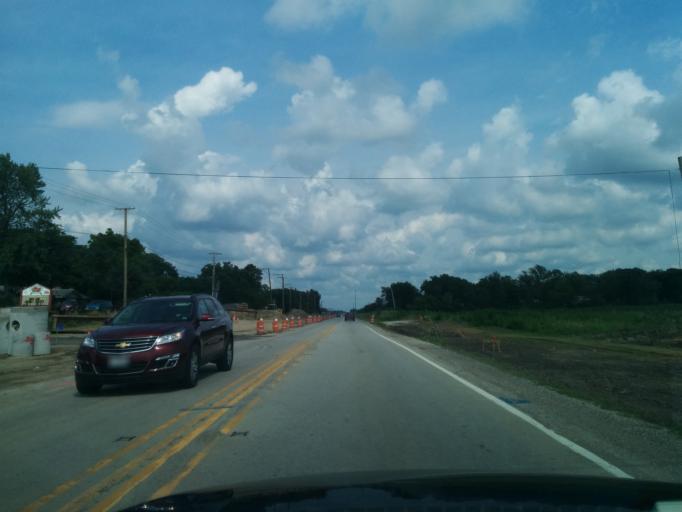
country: US
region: Illinois
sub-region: Will County
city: Homer Glen
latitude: 41.5992
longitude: -87.9654
